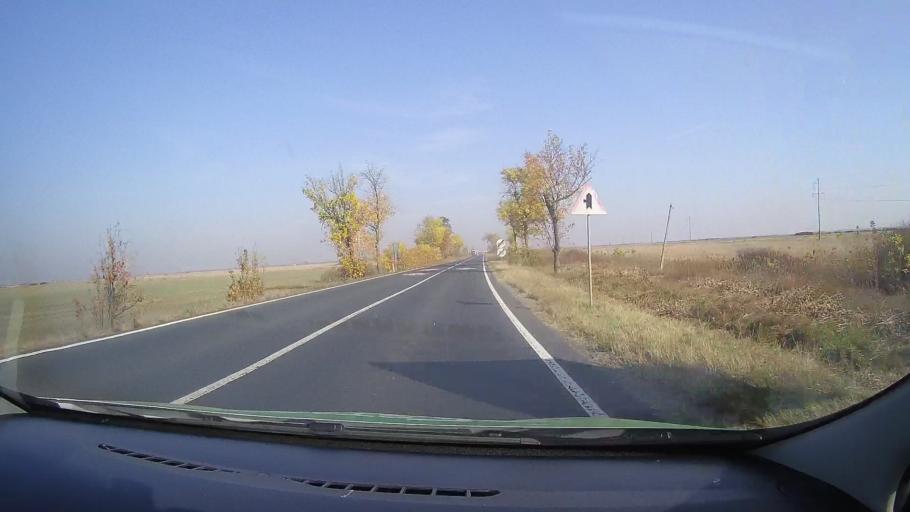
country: RO
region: Arad
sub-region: Comuna Zerind
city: Zerind
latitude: 46.5984
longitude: 21.5260
